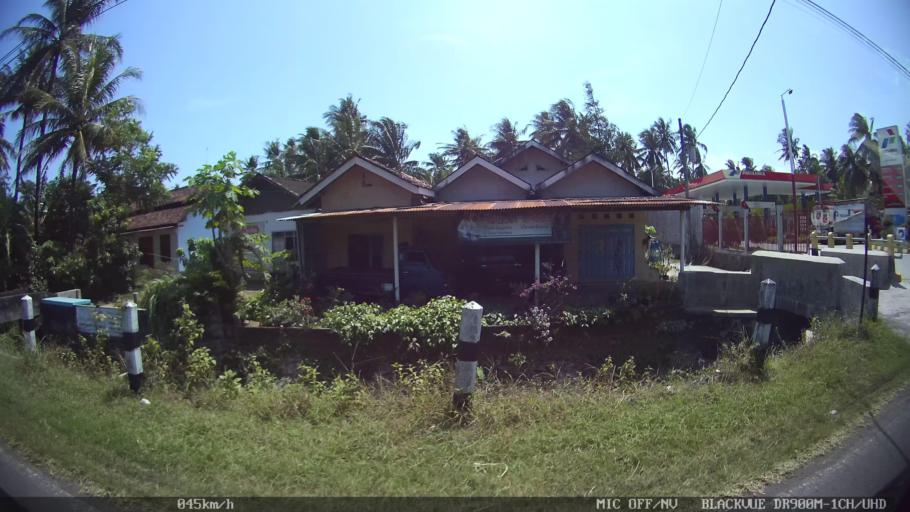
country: ID
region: Daerah Istimewa Yogyakarta
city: Srandakan
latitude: -7.9509
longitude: 110.2137
